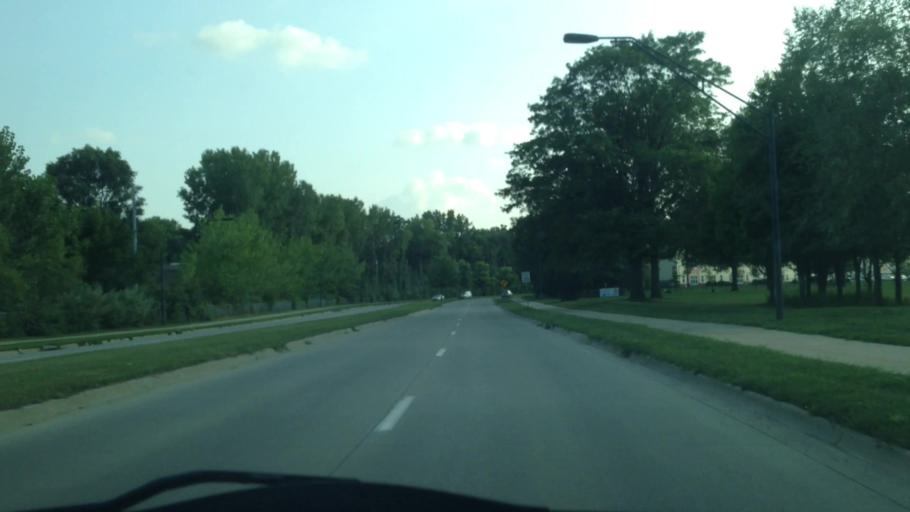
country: US
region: Iowa
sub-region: Johnson County
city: Coralville
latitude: 41.6670
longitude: -91.5689
